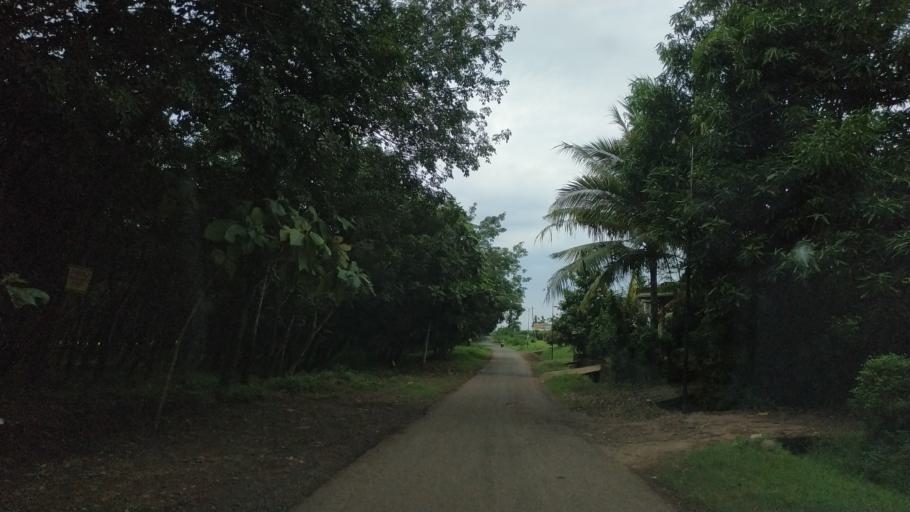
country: ID
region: Central Java
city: Krajan Tegalombo
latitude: -6.4304
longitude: 110.9834
